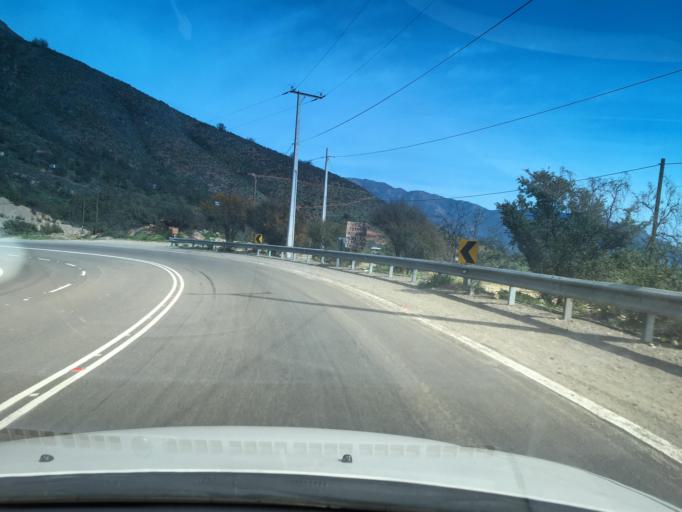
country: CL
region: Valparaiso
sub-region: Provincia de San Felipe
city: Llaillay
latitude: -33.0623
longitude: -71.0241
